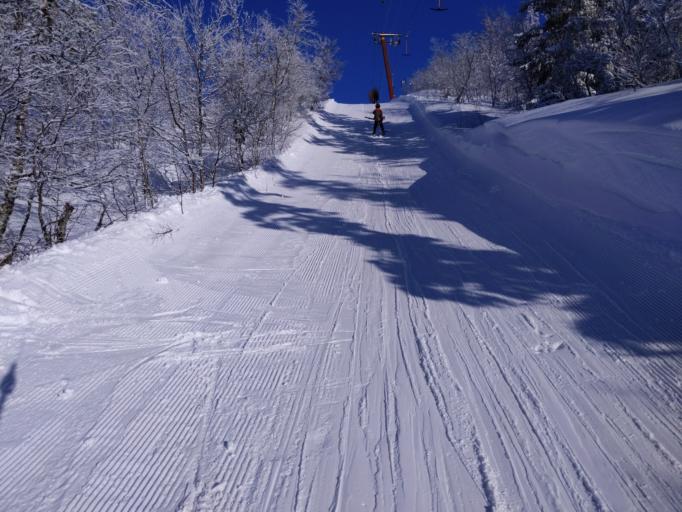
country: SE
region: Jaemtland
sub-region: Harjedalens Kommun
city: Sveg
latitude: 62.4323
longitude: 13.9605
